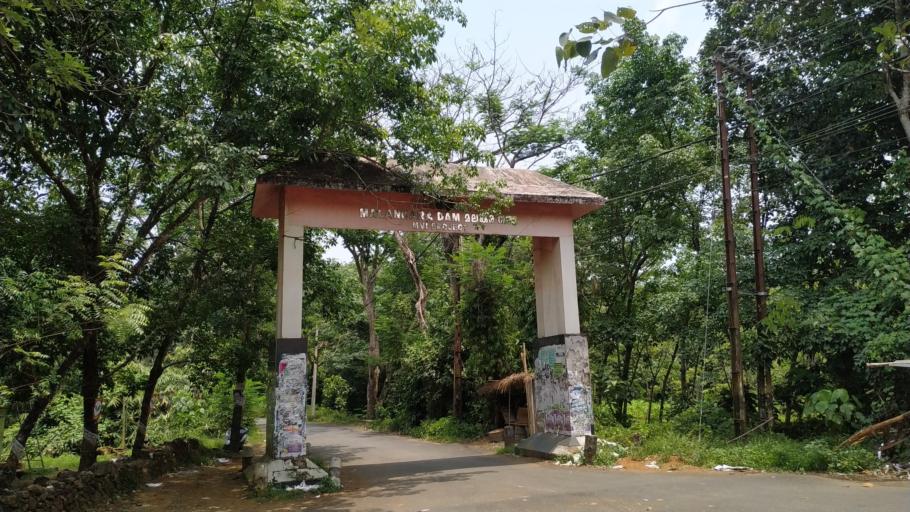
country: IN
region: Kerala
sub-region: Kottayam
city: Lalam
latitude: 9.8533
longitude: 76.7373
